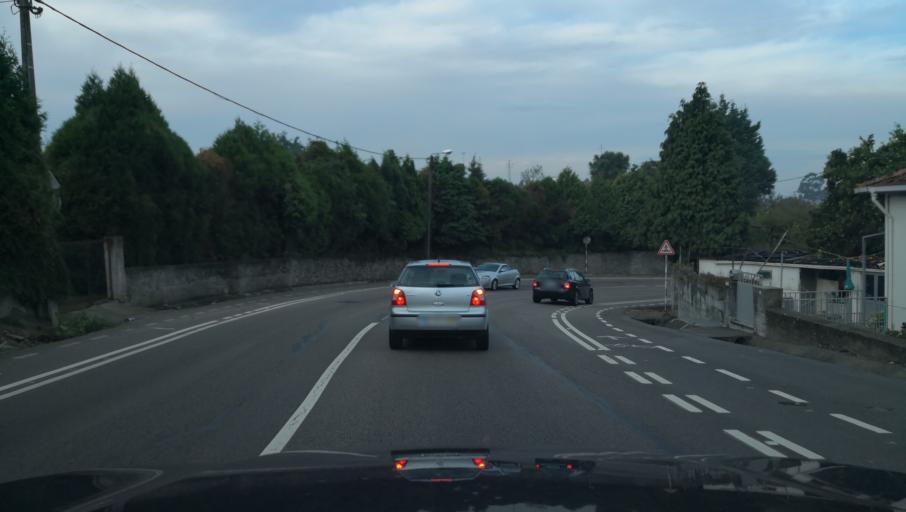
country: PT
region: Porto
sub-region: Gondomar
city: Valbom
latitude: 41.1443
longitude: -8.5655
